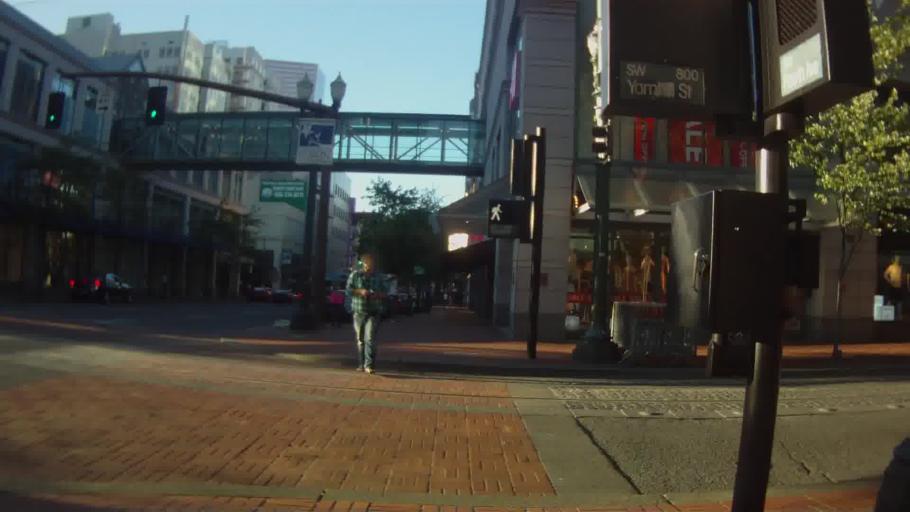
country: US
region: Oregon
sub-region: Multnomah County
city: Portland
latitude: 45.5178
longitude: -122.6768
